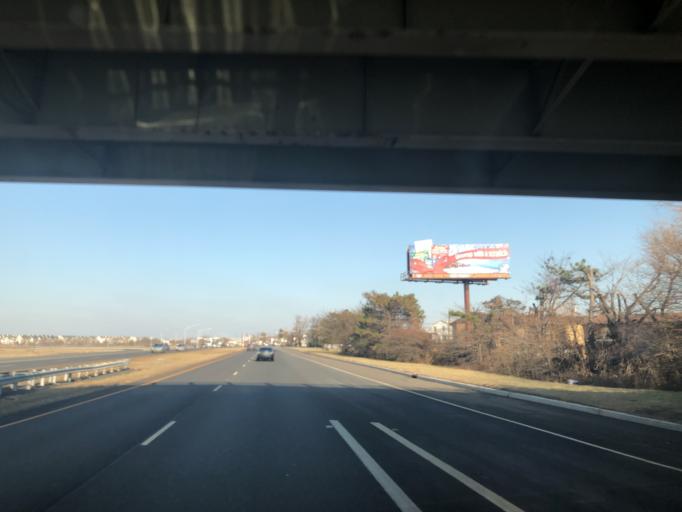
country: US
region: New Jersey
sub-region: Hudson County
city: Bayonne
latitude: 40.6961
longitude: -74.1072
